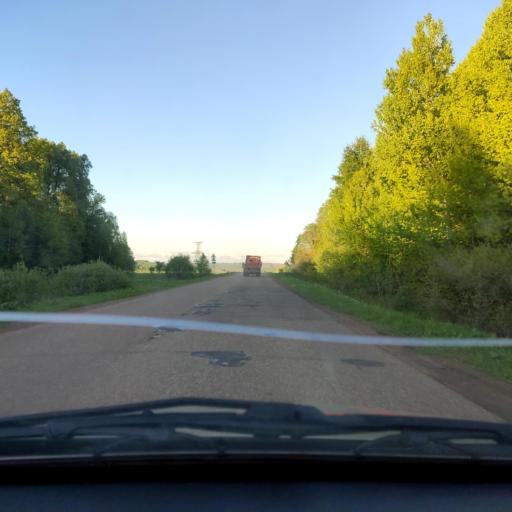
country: RU
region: Bashkortostan
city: Blagoveshchensk
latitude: 55.0417
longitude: 56.1381
